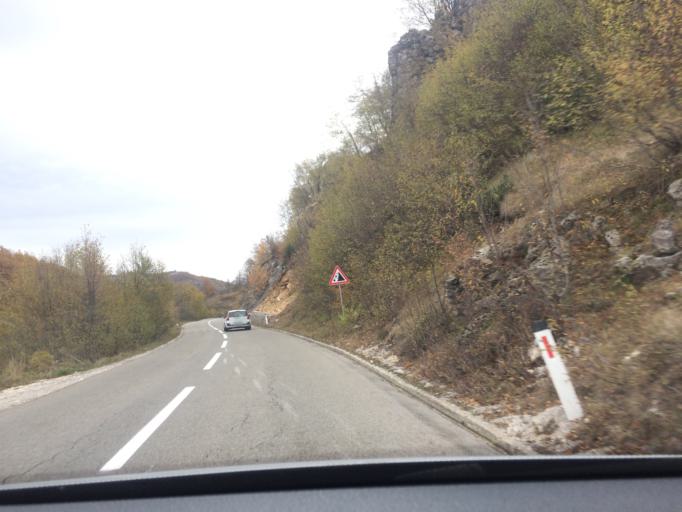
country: ME
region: Opstina Savnik
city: Savnik
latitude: 42.9491
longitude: 19.0833
